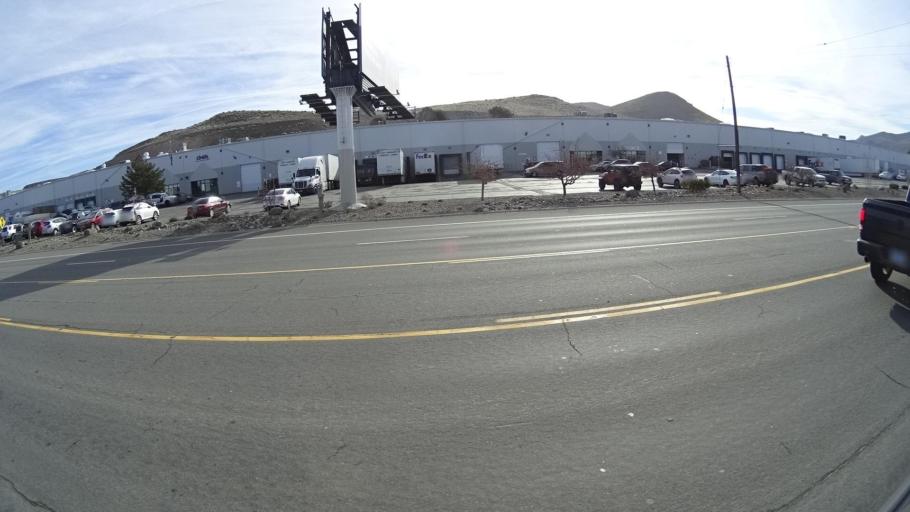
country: US
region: Nevada
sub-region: Washoe County
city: Sparks
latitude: 39.5342
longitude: -119.7040
